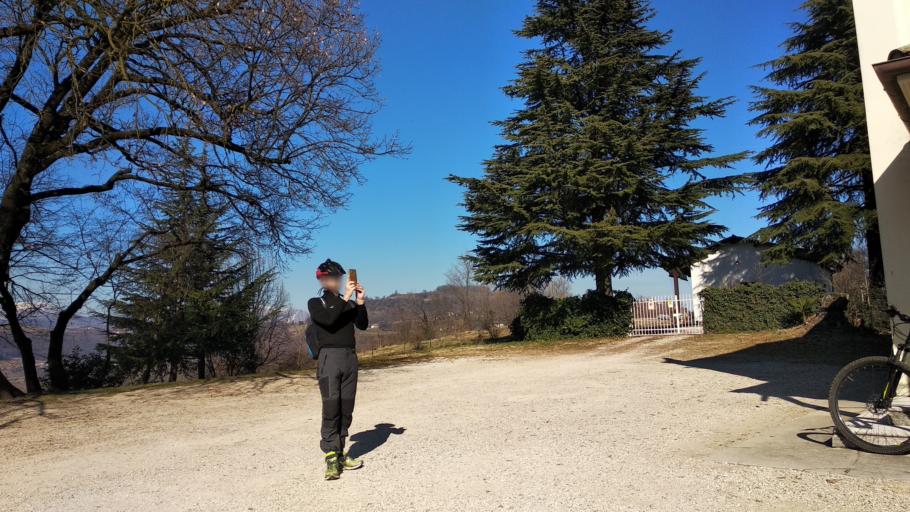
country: IT
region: Veneto
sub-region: Provincia di Vicenza
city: Gambugliano
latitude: 45.5844
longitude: 11.4559
